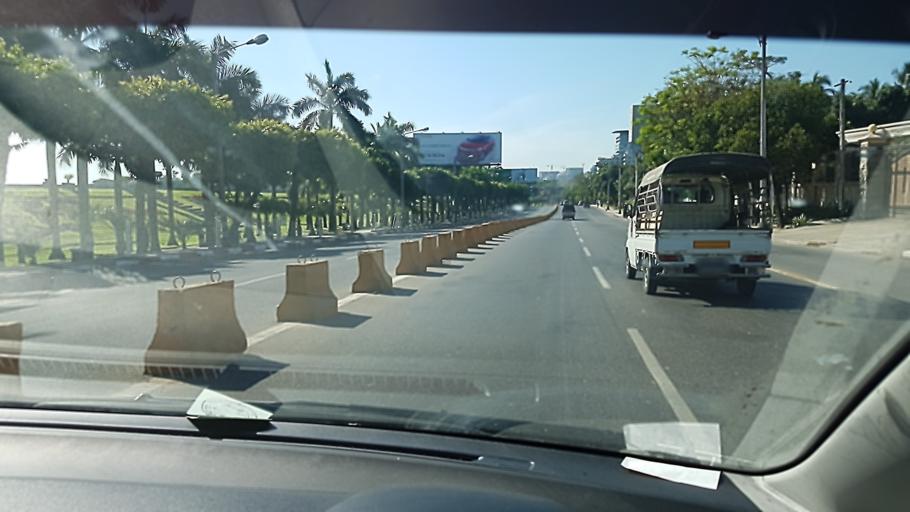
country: MM
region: Yangon
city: Yangon
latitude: 16.8412
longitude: 96.1352
